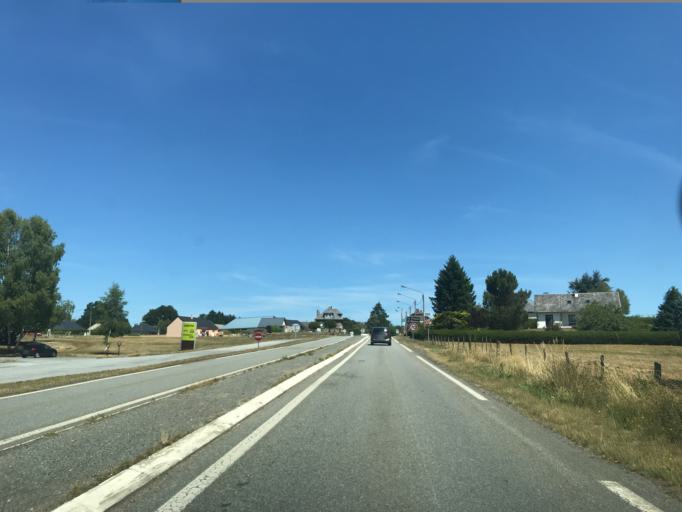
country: FR
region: Limousin
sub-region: Departement de la Correze
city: Meymac
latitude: 45.4654
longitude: 2.1415
